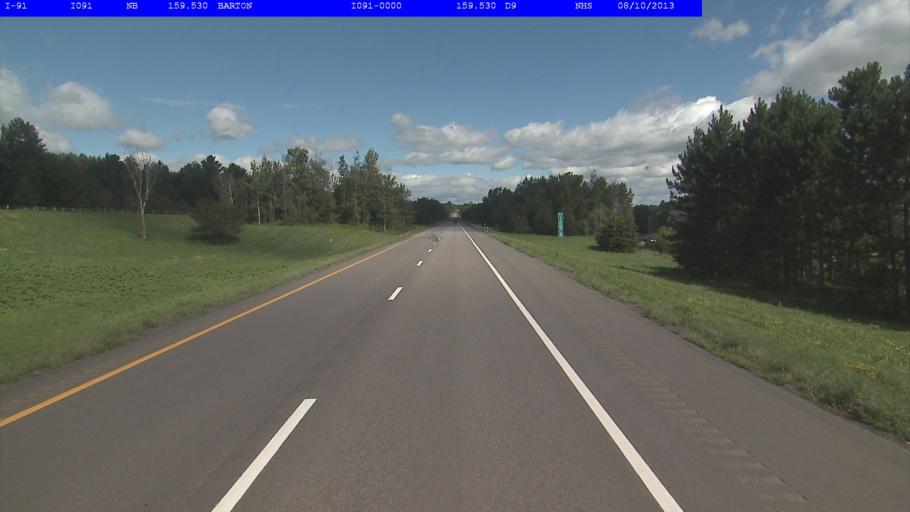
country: US
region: Vermont
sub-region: Orleans County
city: Newport
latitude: 44.7796
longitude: -72.2148
